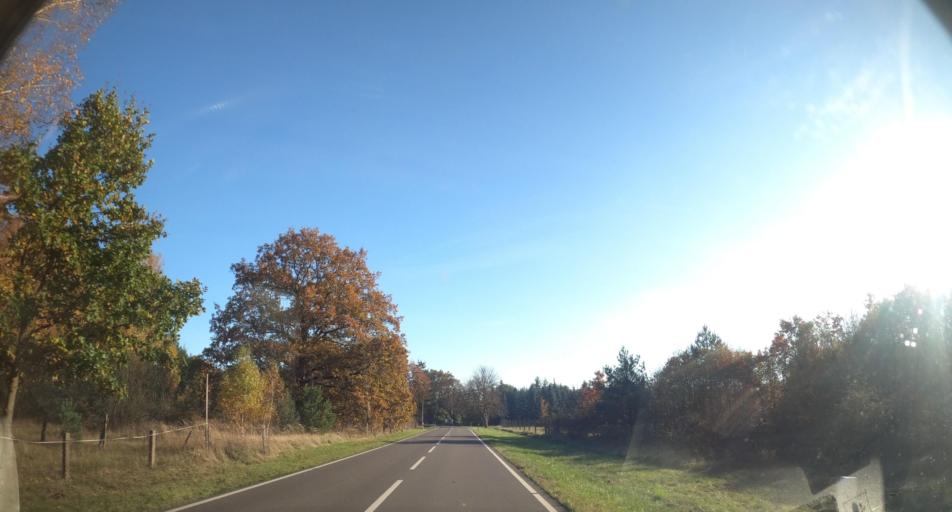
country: DE
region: Mecklenburg-Vorpommern
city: Ahlbeck
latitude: 53.6412
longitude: 14.2057
